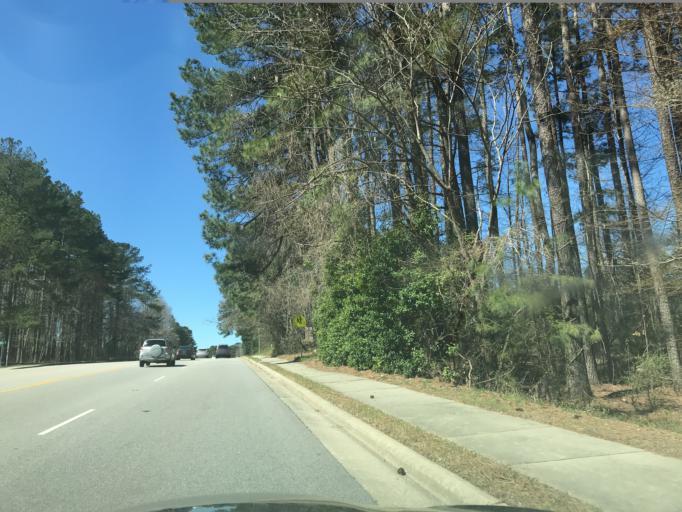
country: US
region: North Carolina
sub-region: Wake County
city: Garner
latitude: 35.6863
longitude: -78.6120
